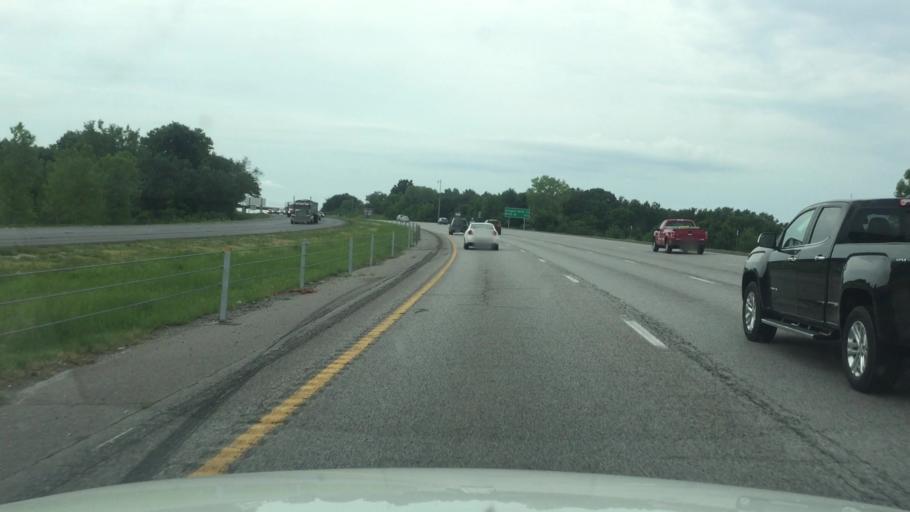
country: US
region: Missouri
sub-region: Jackson County
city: Raytown
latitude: 39.0077
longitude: -94.5011
